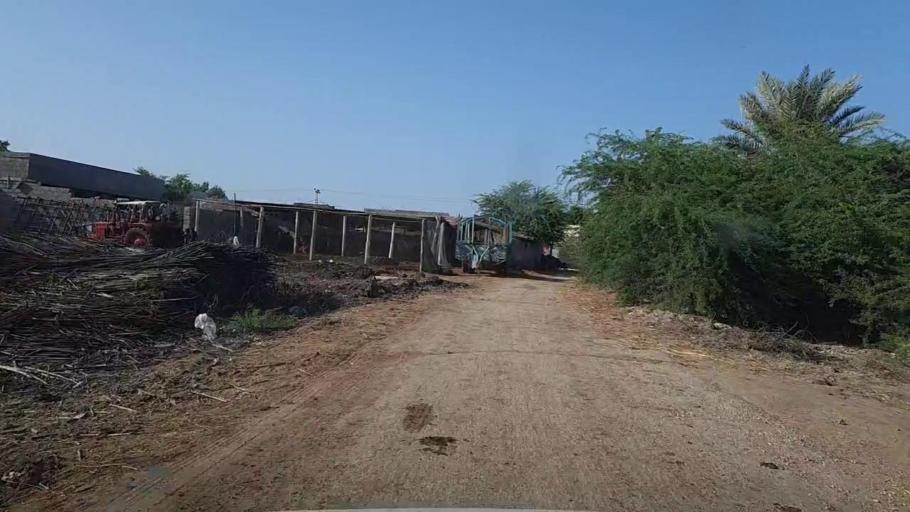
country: PK
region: Sindh
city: Kario
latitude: 24.5980
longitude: 68.5278
